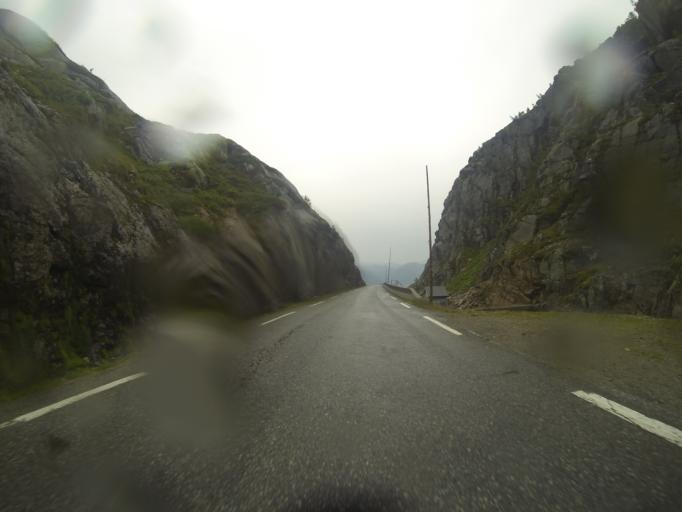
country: NO
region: Hordaland
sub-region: Odda
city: Odda
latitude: 59.7785
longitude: 6.7517
